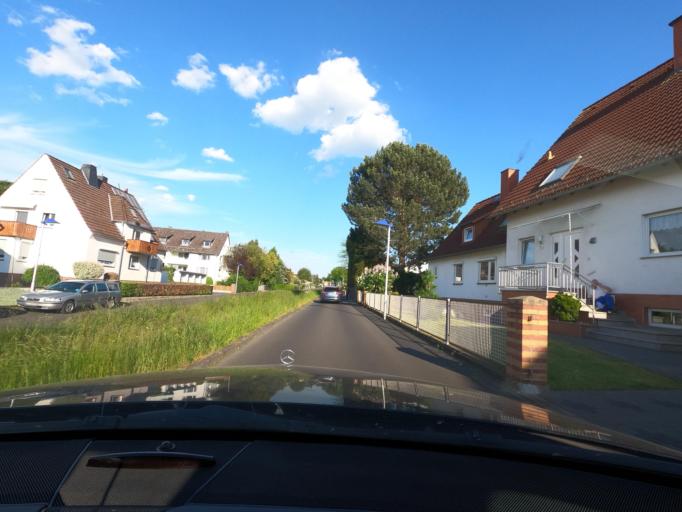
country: DE
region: Hesse
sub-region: Regierungsbezirk Kassel
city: Lohfelden
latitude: 51.3054
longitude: 9.5511
